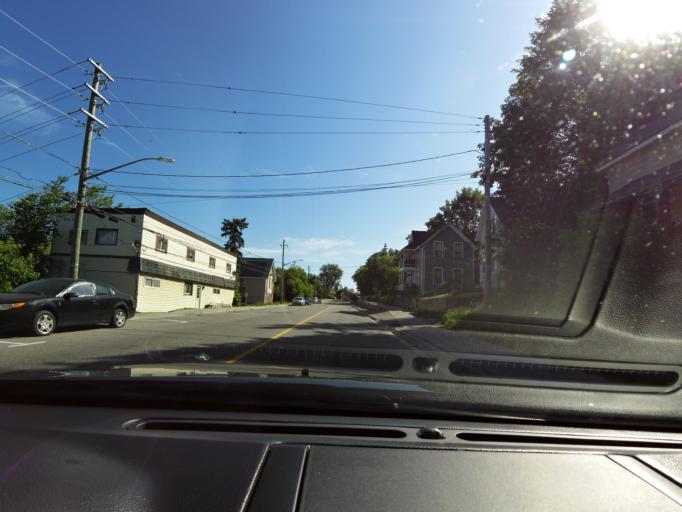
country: CA
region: Ontario
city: Huntsville
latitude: 45.3244
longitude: -79.2240
